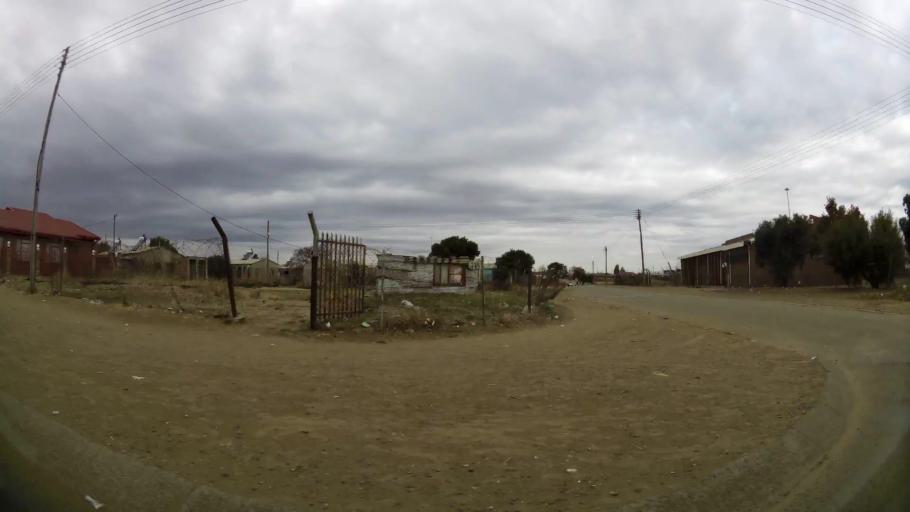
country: ZA
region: Orange Free State
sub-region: Fezile Dabi District Municipality
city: Kroonstad
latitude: -27.6435
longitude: 27.1831
